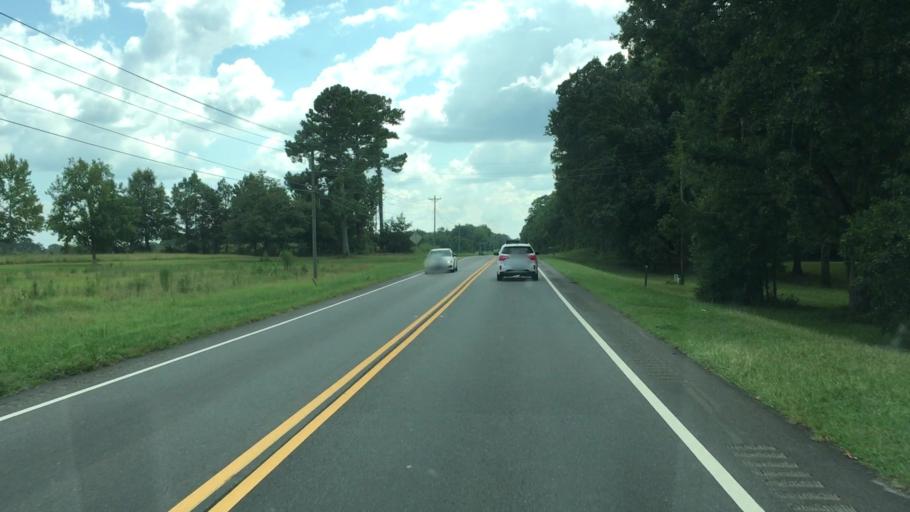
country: US
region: Georgia
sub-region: Putnam County
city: Eatonton
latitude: 33.3727
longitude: -83.3812
